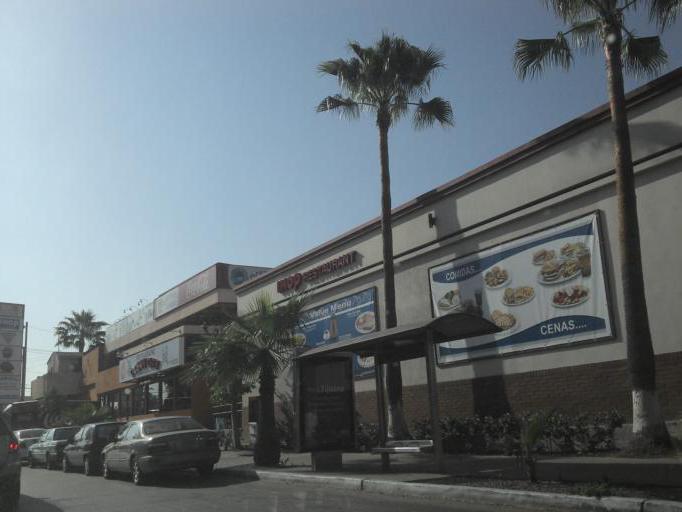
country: MX
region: Baja California
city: Tijuana
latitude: 32.5168
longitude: -117.0078
